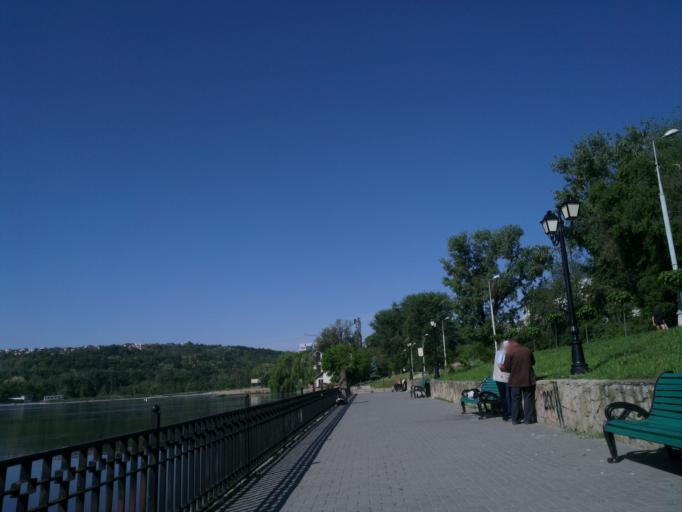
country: MD
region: Chisinau
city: Chisinau
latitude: 47.0206
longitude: 28.8128
